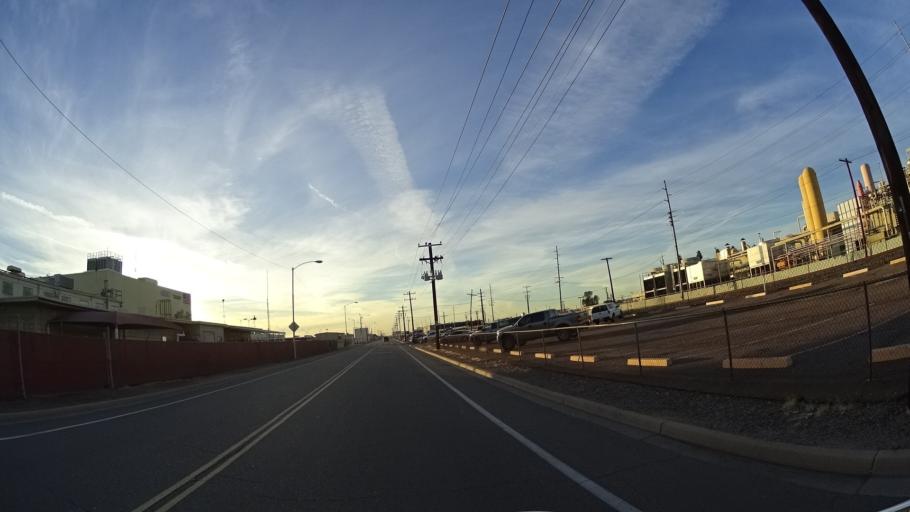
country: US
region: Arizona
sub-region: Maricopa County
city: Phoenix
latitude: 33.4440
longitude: -112.0058
